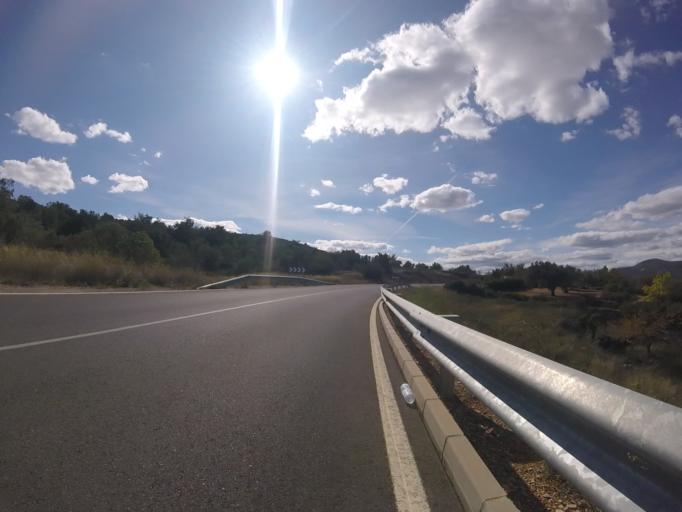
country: ES
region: Valencia
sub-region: Provincia de Castello
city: Cati
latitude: 40.4287
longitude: 0.0920
